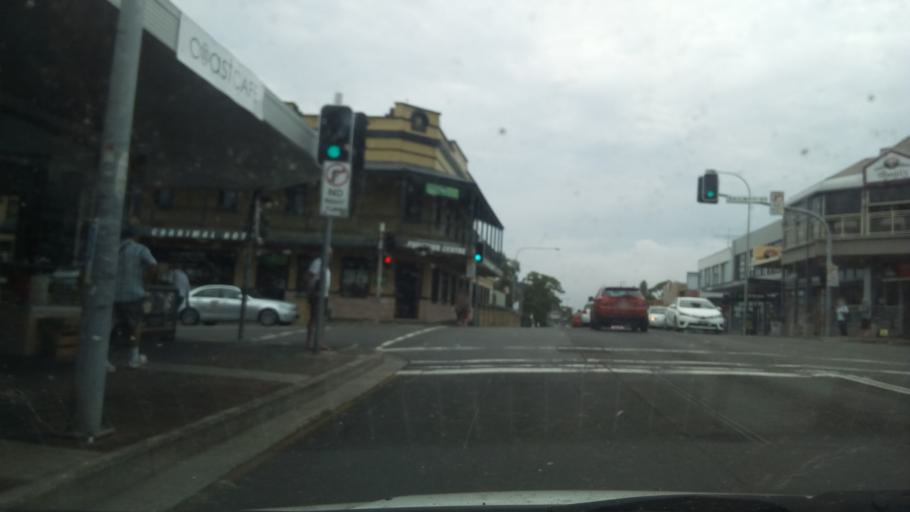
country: AU
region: New South Wales
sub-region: Wollongong
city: Corrimal
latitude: -34.3730
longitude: 150.8970
